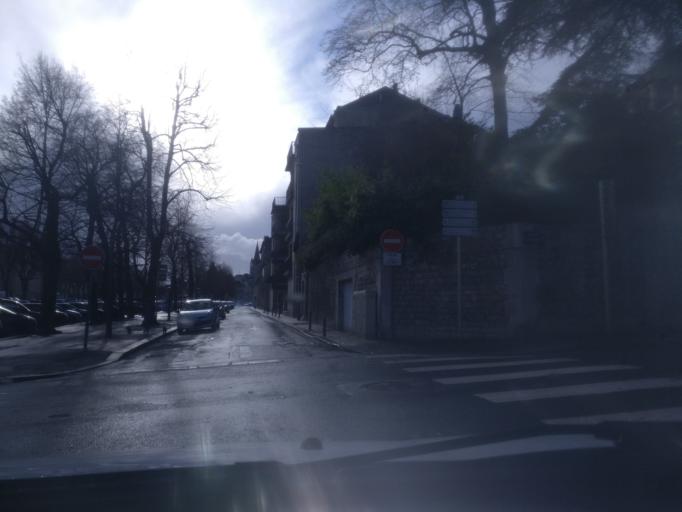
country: FR
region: Lower Normandy
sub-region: Departement du Calvados
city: Caen
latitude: 49.1856
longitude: -0.3682
